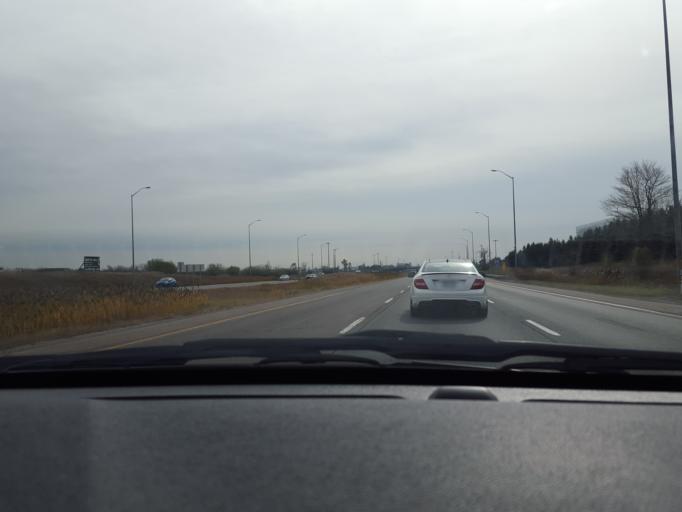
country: CA
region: Ontario
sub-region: York
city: Richmond Hill
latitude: 43.8906
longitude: -79.3820
